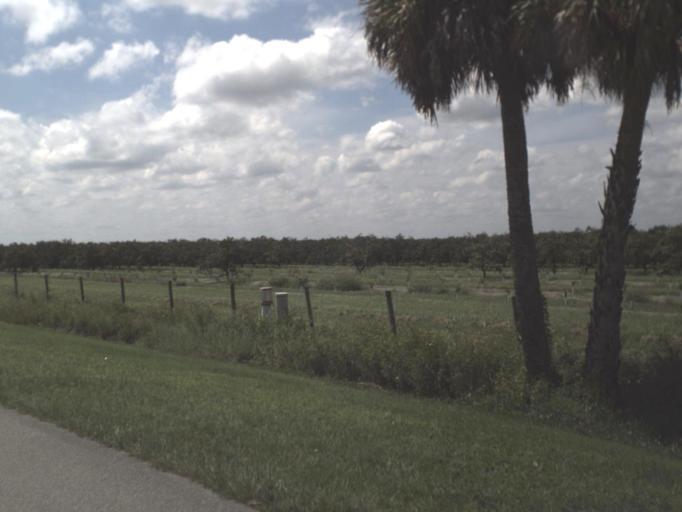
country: US
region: Florida
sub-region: Collier County
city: Immokalee
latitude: 26.5396
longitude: -81.4355
